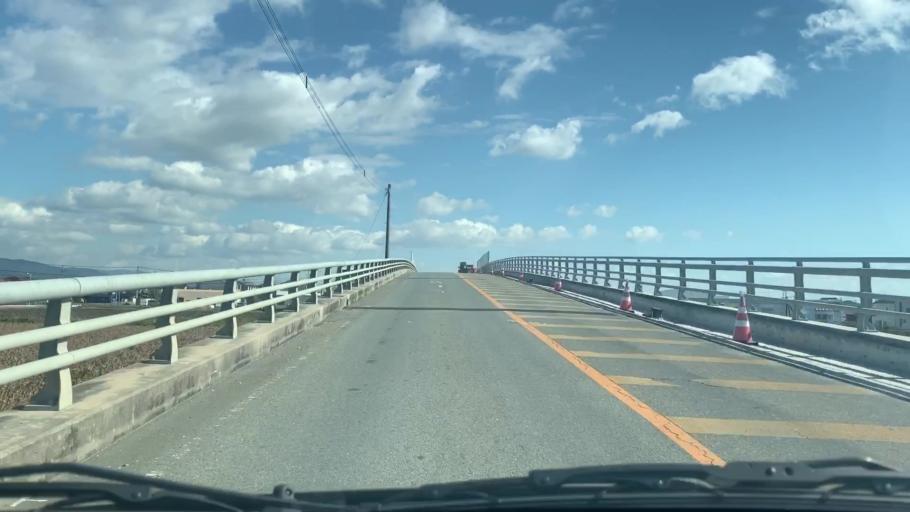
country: JP
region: Saga Prefecture
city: Saga-shi
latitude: 33.2767
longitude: 130.2123
